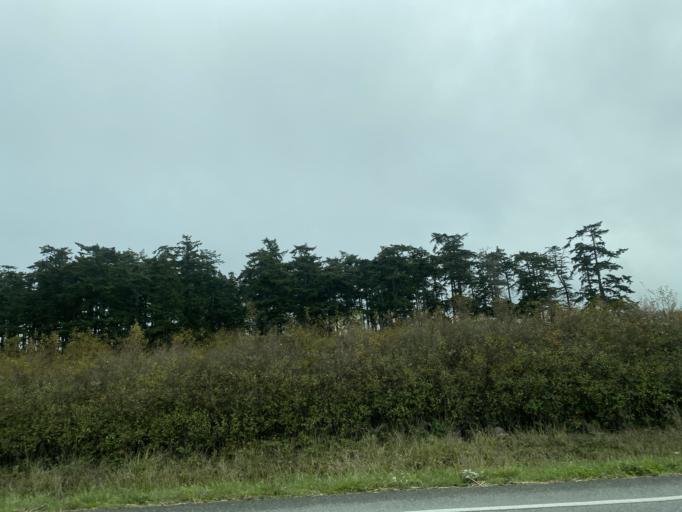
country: US
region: Washington
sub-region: Island County
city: Coupeville
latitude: 48.2106
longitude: -122.6931
